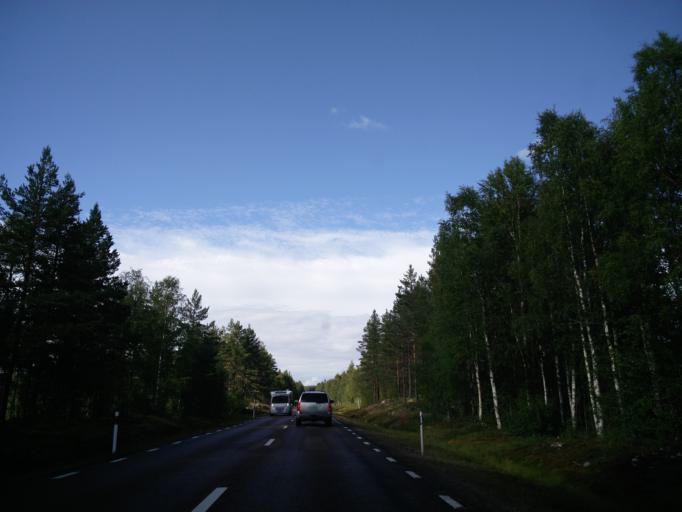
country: SE
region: Vaermland
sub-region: Hagfors Kommun
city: Ekshaerad
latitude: 60.4658
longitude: 13.3002
